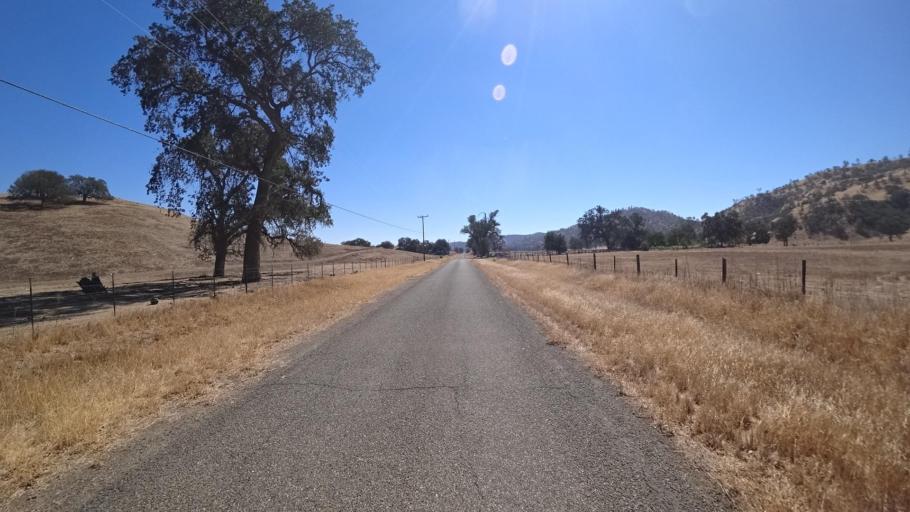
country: US
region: California
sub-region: Monterey County
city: King City
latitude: 36.1358
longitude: -120.7483
